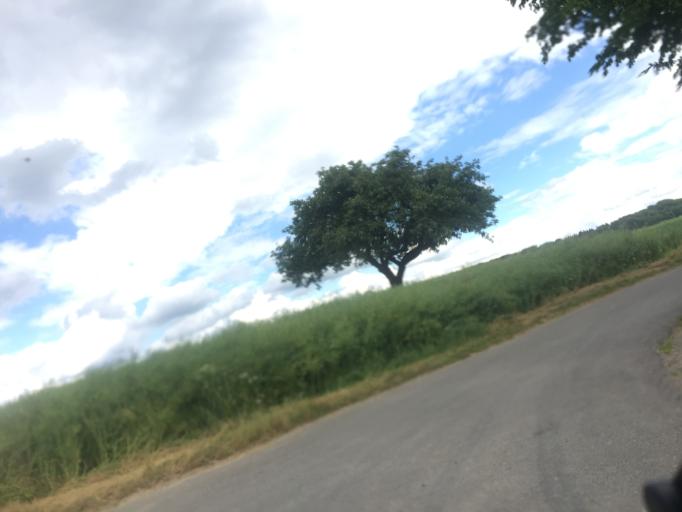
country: DE
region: Rheinland-Pfalz
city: Girod
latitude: 50.4567
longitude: 7.9008
